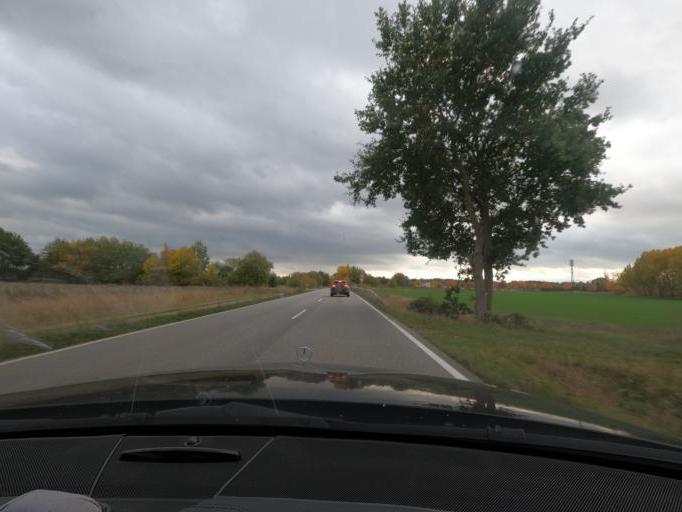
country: DE
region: Schleswig-Holstein
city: Geesthacht
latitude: 53.4581
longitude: 10.3694
